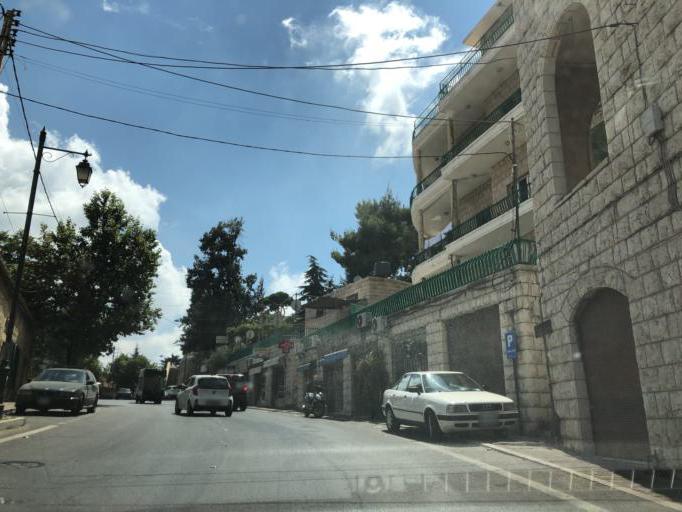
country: LB
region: Mont-Liban
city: Beit ed Dine
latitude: 33.6981
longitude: 35.5620
